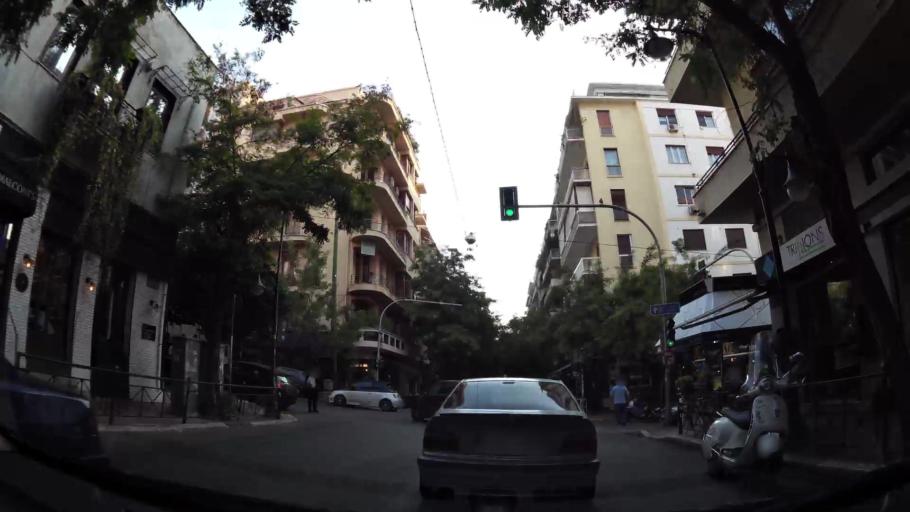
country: GR
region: Attica
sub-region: Nomarchia Athinas
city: Vyronas
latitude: 37.9782
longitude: 23.7447
